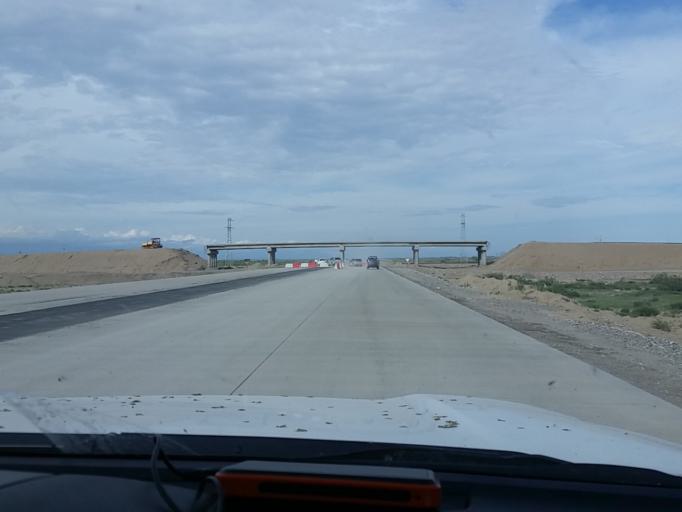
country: KZ
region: Almaty Oblysy
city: Zharkent
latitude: 44.0442
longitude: 79.9793
